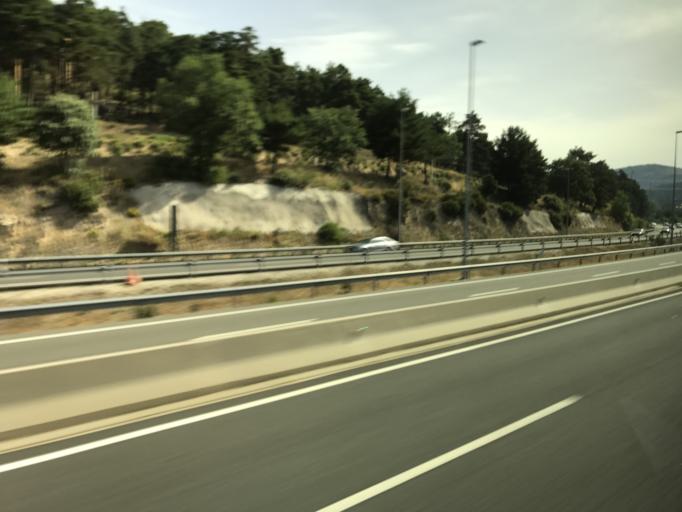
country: ES
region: Madrid
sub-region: Provincia de Madrid
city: Guadarrama
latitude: 40.7128
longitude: -4.1727
